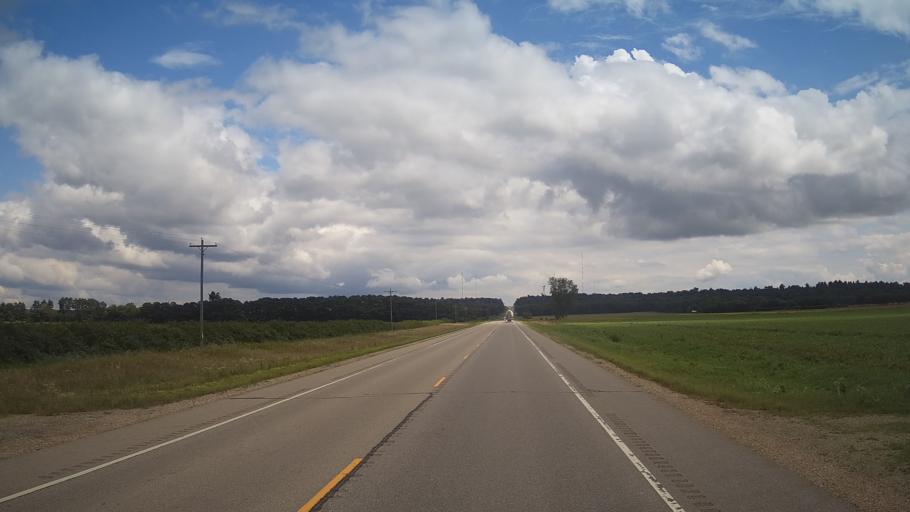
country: US
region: Wisconsin
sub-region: Marquette County
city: Westfield
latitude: 44.0221
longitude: -89.5929
